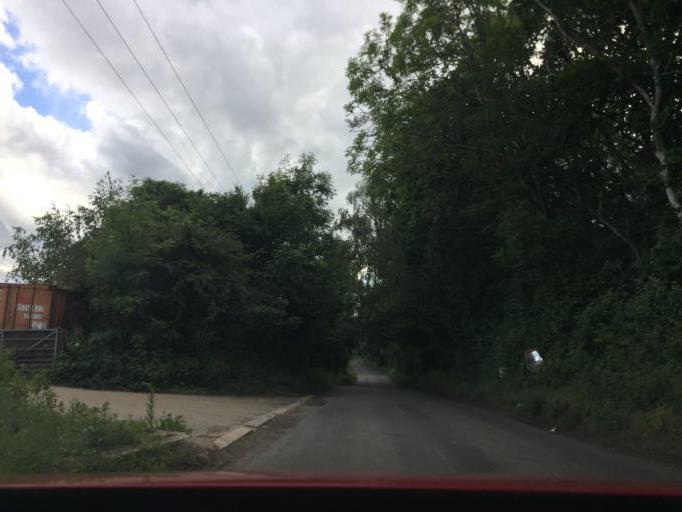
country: GB
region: England
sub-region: Hertfordshire
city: Harpenden
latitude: 51.8599
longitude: -0.3538
